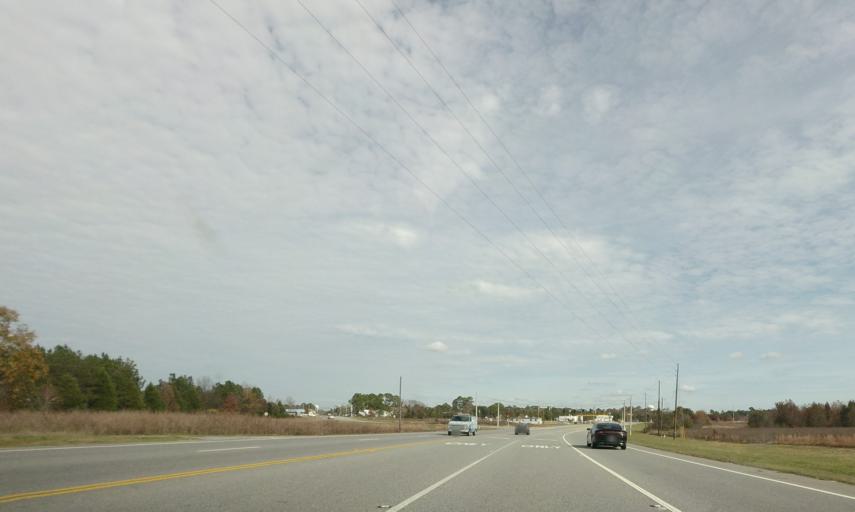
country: US
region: Georgia
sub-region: Laurens County
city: Dublin
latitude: 32.5248
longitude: -82.9453
